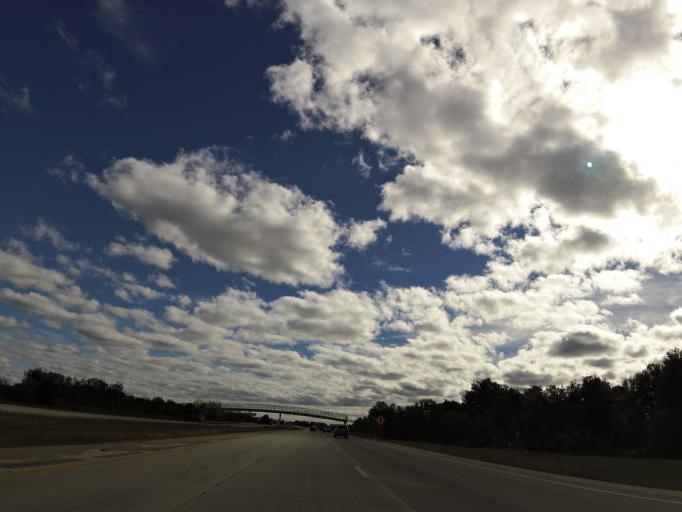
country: US
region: Michigan
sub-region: Genesee County
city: Burton
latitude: 43.0195
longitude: -83.5924
